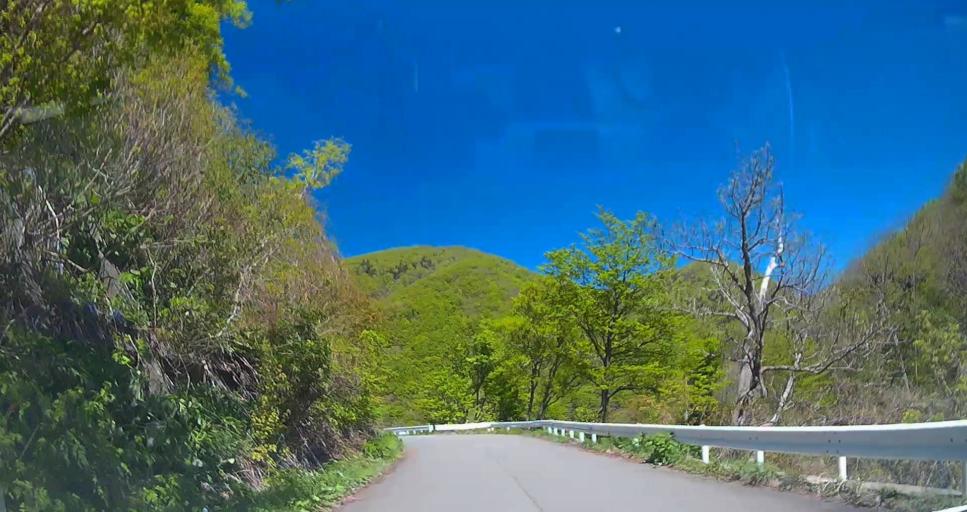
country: JP
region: Aomori
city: Mutsu
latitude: 41.3229
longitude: 140.8166
